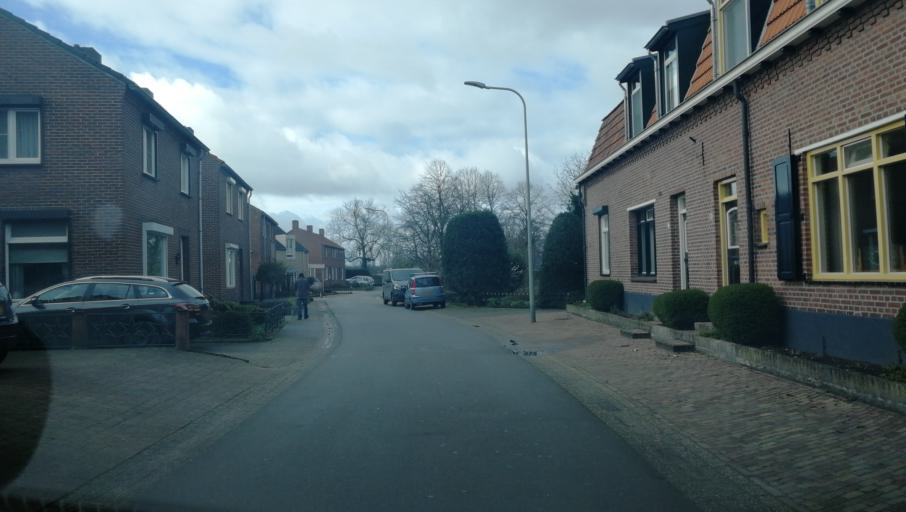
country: NL
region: Limburg
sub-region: Gemeente Venlo
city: Venlo
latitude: 51.4133
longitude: 6.1622
